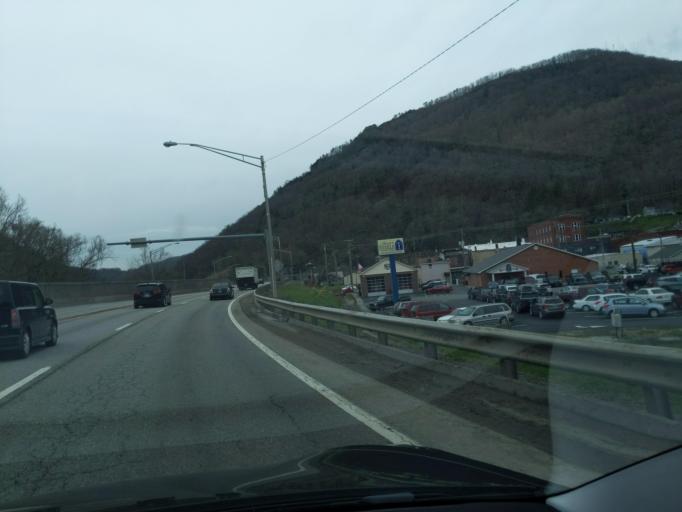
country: US
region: Kentucky
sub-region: Bell County
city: Pineville
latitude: 36.7620
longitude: -83.6931
